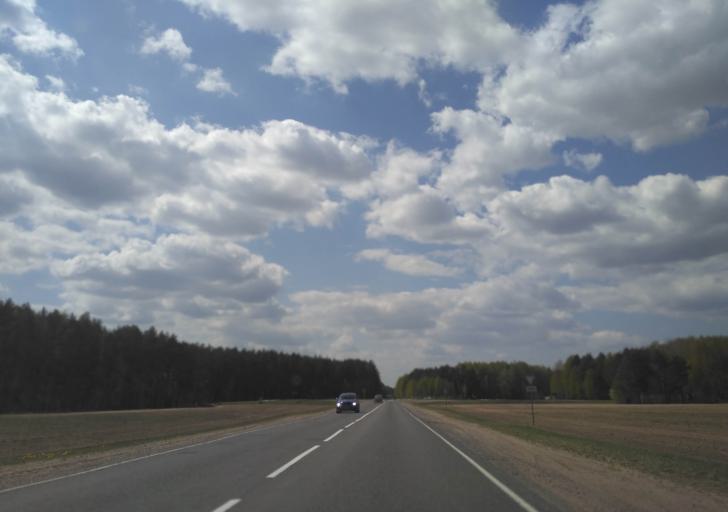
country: BY
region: Minsk
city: Vilyeyka
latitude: 54.5137
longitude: 26.9998
